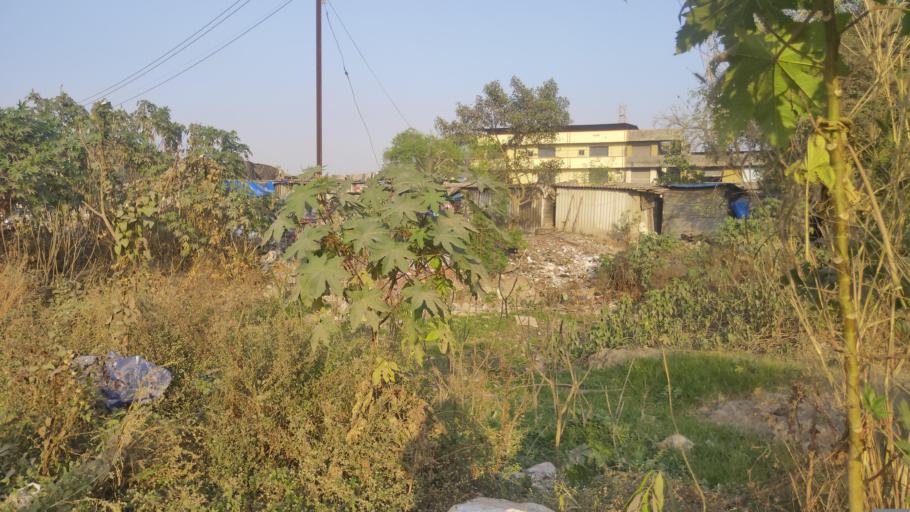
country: IN
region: Maharashtra
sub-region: Thane
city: Bhiwandi
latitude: 19.2512
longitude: 73.0285
